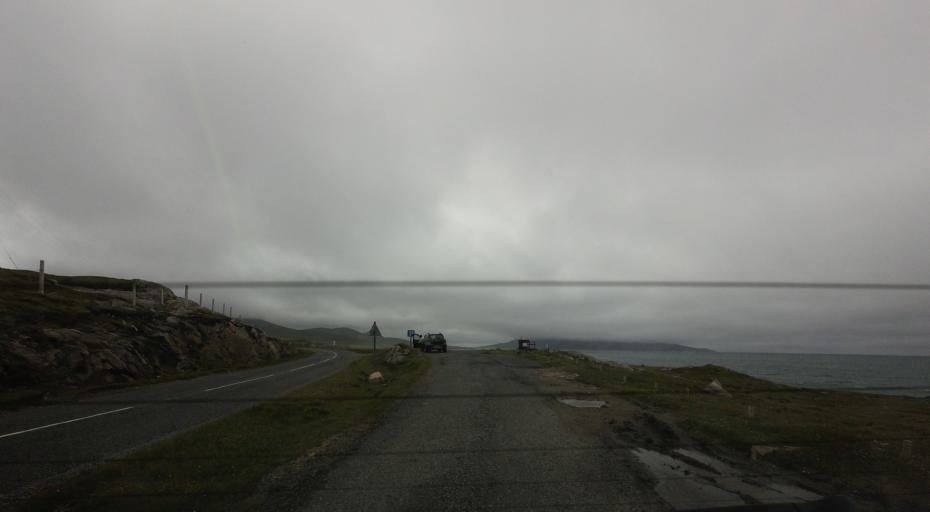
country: GB
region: Scotland
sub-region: Eilean Siar
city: Harris
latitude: 57.8549
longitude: -6.9996
